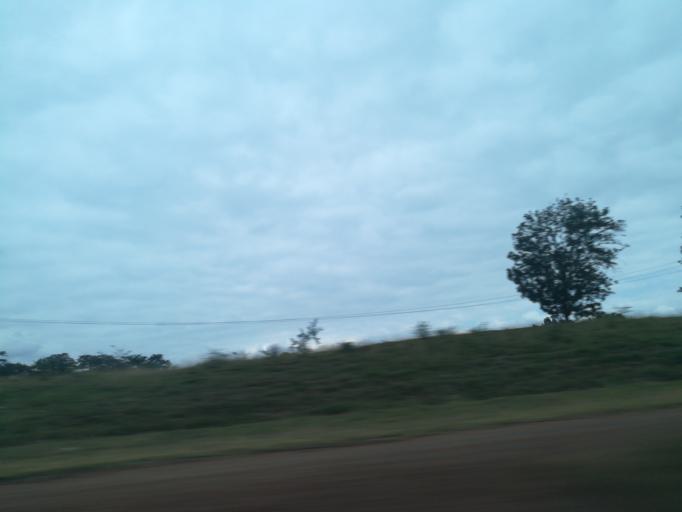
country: KE
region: Nairobi Area
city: Thika
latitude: -1.0784
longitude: 37.0449
